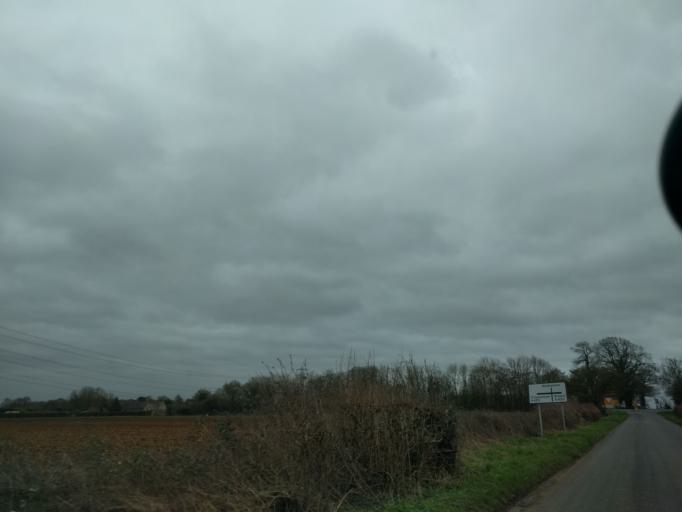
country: GB
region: England
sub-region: Wiltshire
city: Biddestone
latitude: 51.4728
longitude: -2.1966
